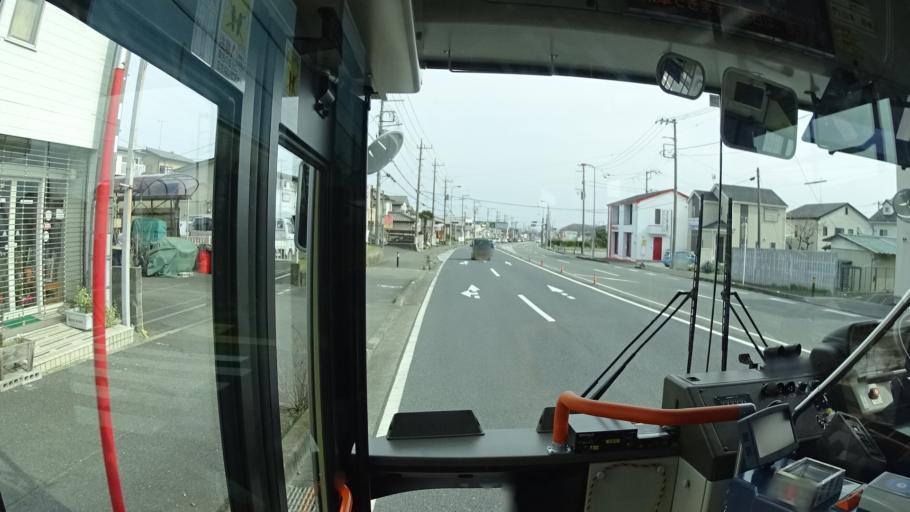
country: JP
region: Kanagawa
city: Atsugi
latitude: 35.4913
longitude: 139.3213
